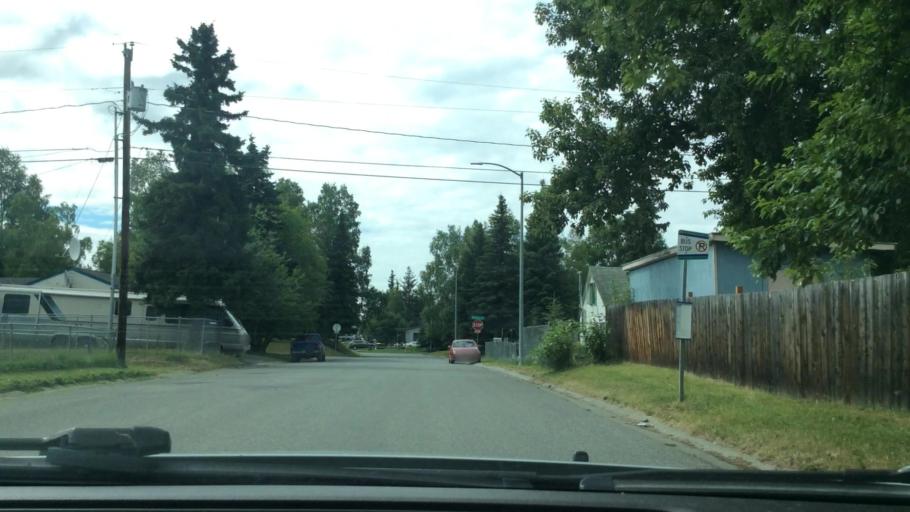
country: US
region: Alaska
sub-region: Anchorage Municipality
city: Anchorage
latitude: 61.2202
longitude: -149.7883
